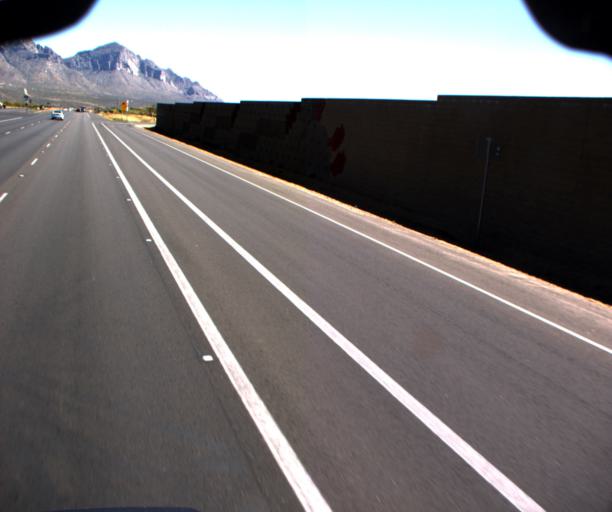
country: US
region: Arizona
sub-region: Pima County
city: Catalina
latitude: 32.4476
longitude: -110.9340
